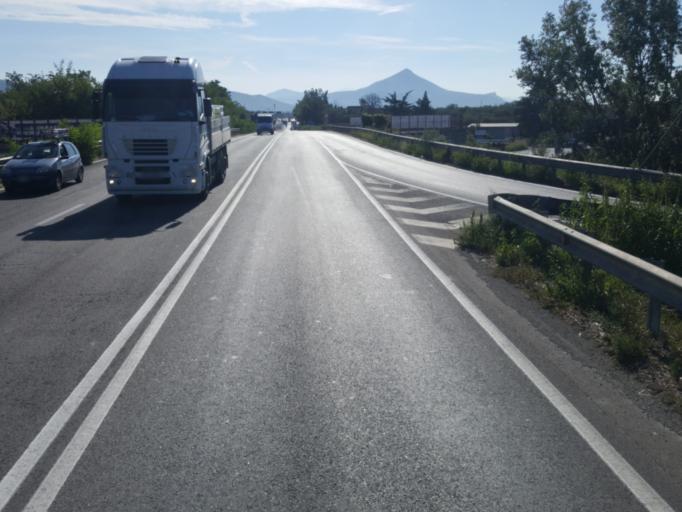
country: IT
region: Campania
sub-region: Provincia di Caserta
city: Pignataro Maggiore
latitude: 41.1630
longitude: 14.1699
